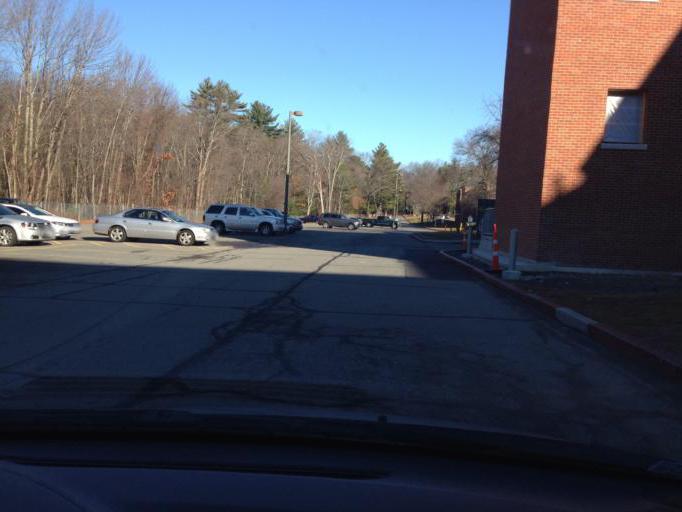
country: US
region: Massachusetts
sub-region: Middlesex County
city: Bedford
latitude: 42.5057
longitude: -71.2763
